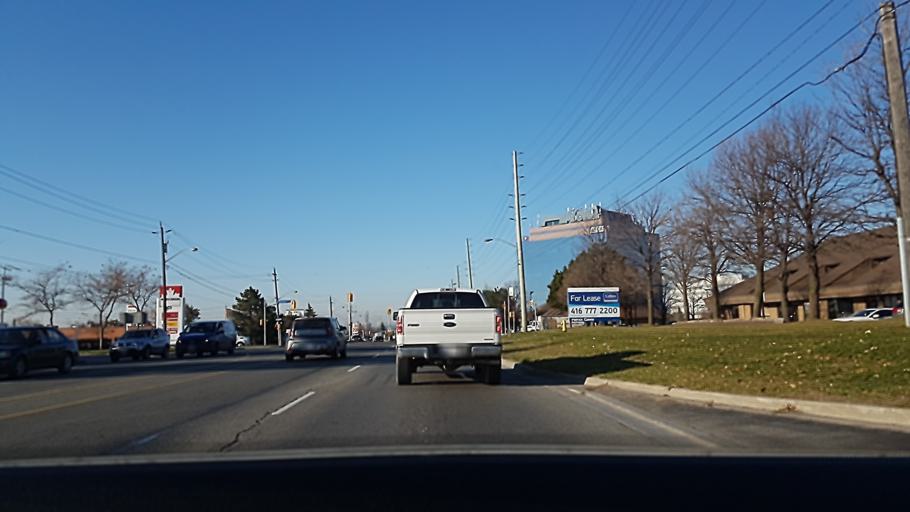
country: CA
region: Ontario
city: Concord
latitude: 43.7720
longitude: -79.5393
